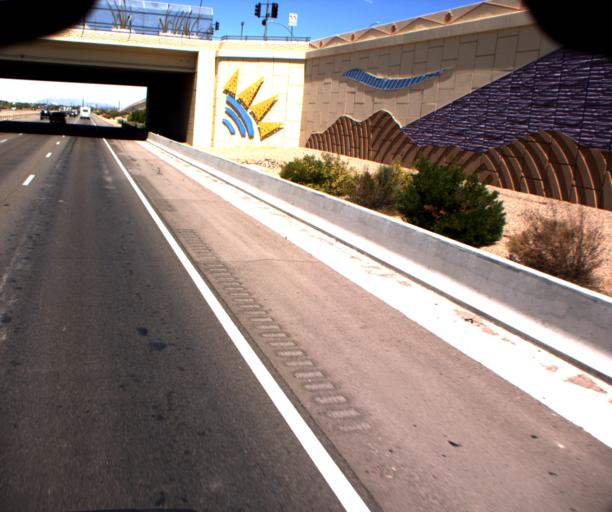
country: US
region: Arizona
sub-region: Pima County
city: Tortolita
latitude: 32.3785
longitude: -111.1089
